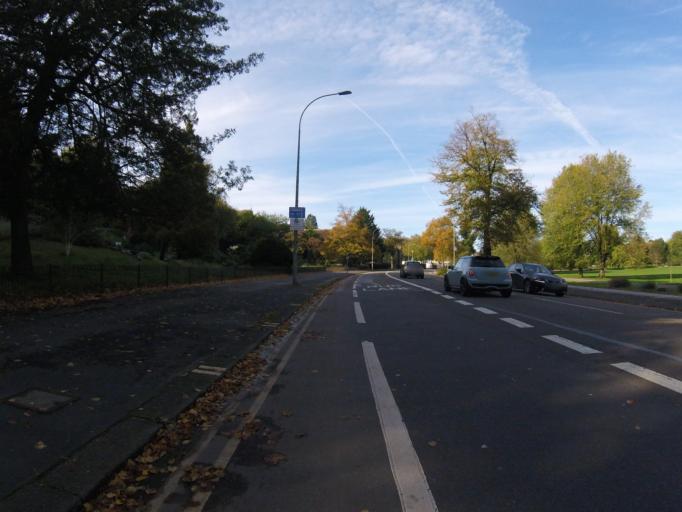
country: GB
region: England
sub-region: Brighton and Hove
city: Brighton
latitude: 50.8395
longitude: -0.1492
